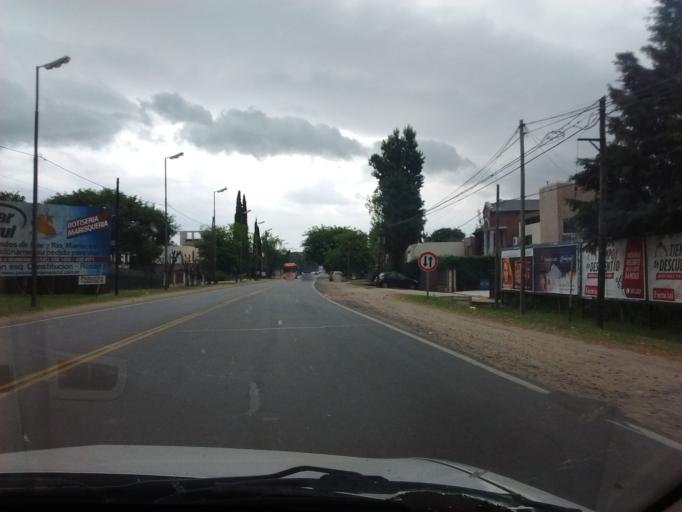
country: AR
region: Santa Fe
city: Funes
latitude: -32.9269
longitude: -60.7477
